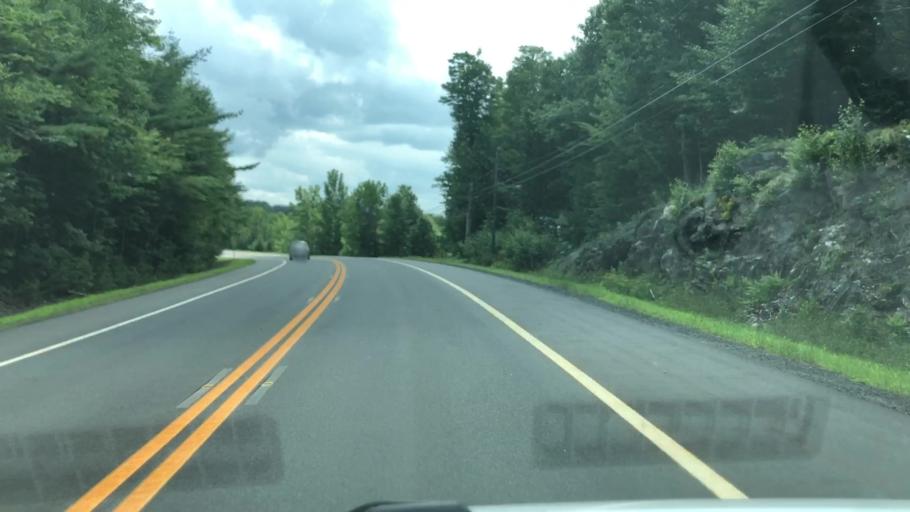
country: US
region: Massachusetts
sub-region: Franklin County
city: Ashfield
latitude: 42.5044
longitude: -72.8115
